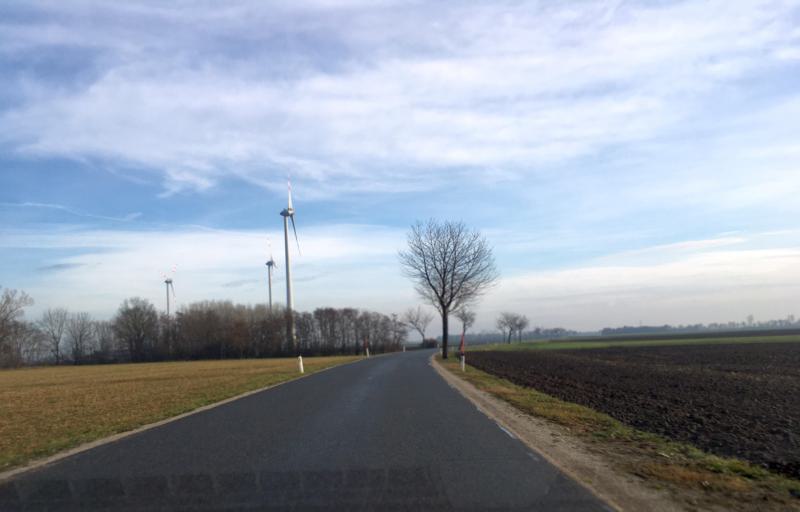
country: AT
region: Lower Austria
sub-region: Politischer Bezirk Ganserndorf
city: Andlersdorf
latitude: 48.1942
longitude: 16.6714
